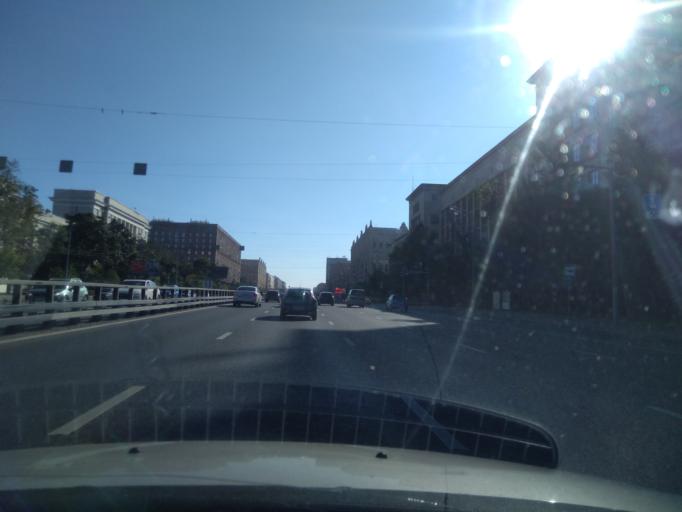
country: RU
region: Moscow
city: Ostankinskiy
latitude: 55.8161
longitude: 37.6384
